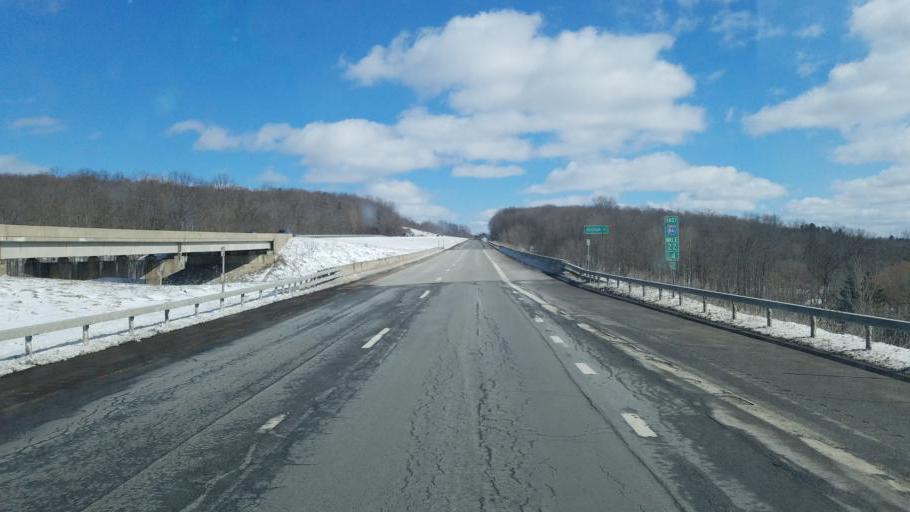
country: US
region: New York
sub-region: Chautauqua County
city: Lakewood
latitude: 42.1378
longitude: -79.3462
